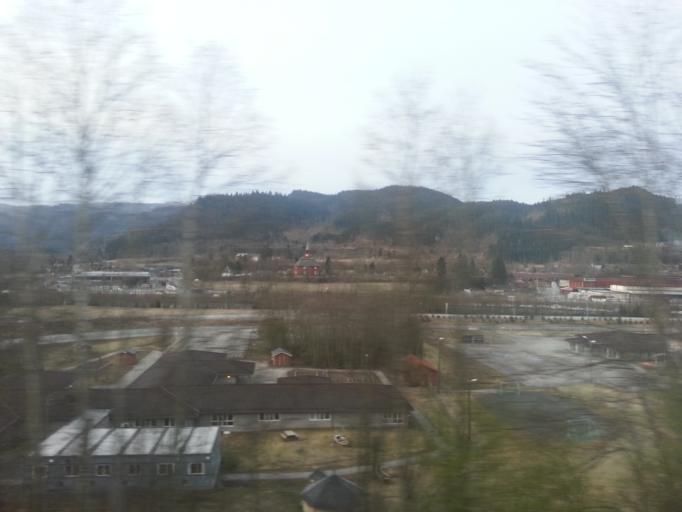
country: NO
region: Sor-Trondelag
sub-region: Midtre Gauldal
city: Storen
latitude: 63.0349
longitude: 10.2873
